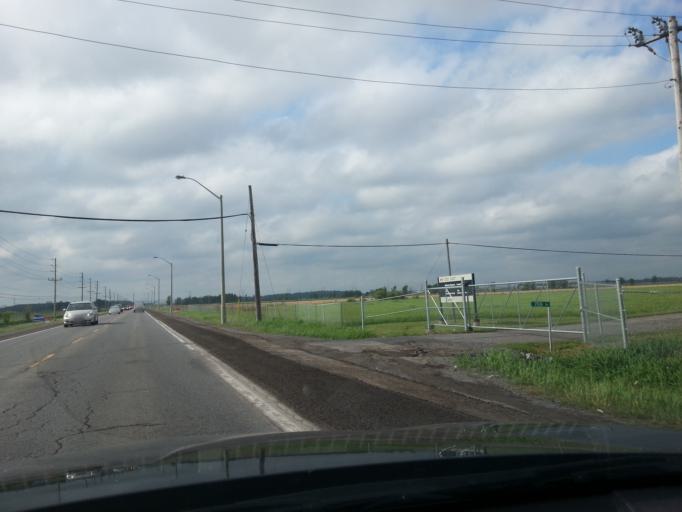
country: CA
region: Ontario
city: Bells Corners
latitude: 45.2934
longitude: -75.7601
